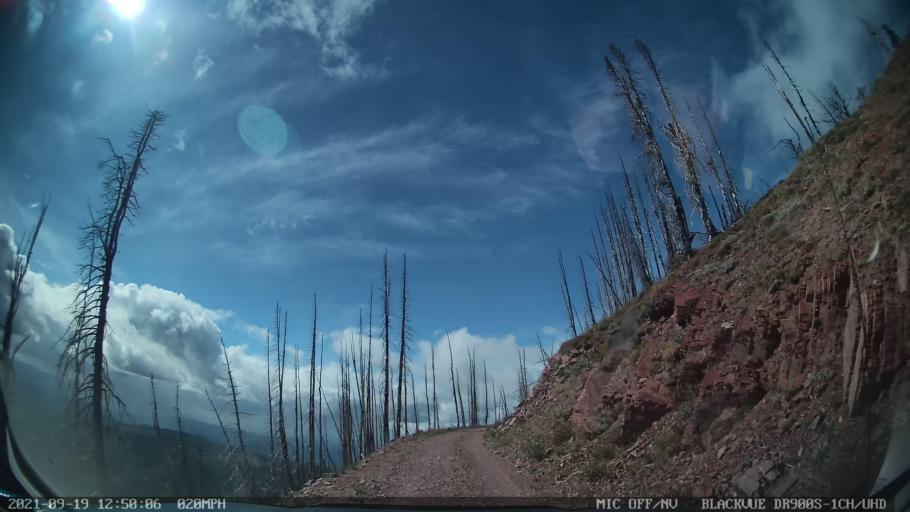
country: US
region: Montana
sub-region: Missoula County
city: Seeley Lake
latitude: 47.1851
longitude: -113.3552
